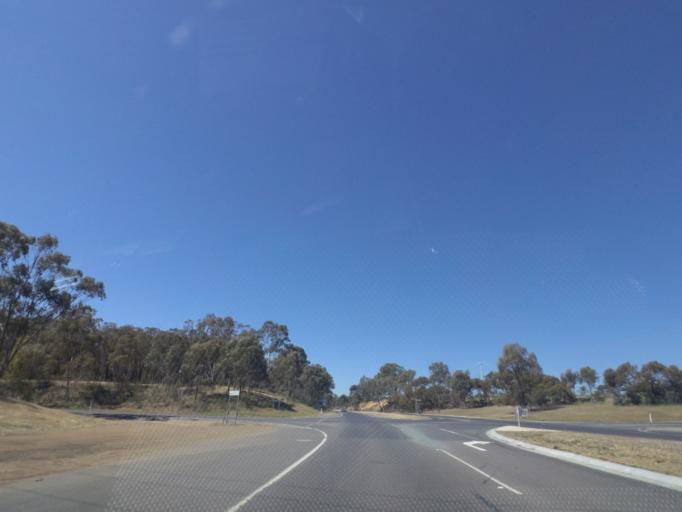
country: AU
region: Victoria
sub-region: Murrindindi
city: Kinglake West
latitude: -37.0301
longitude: 145.1039
